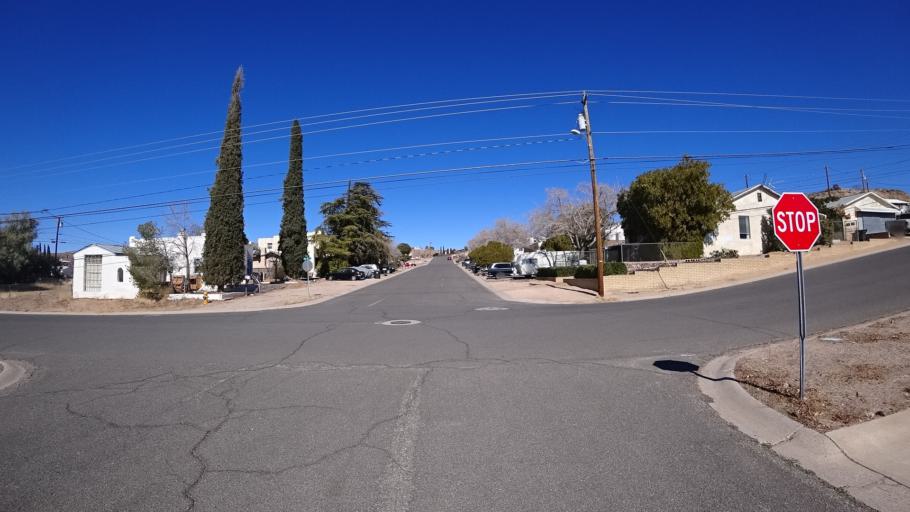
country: US
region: Arizona
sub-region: Mohave County
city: Kingman
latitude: 35.1944
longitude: -114.0588
